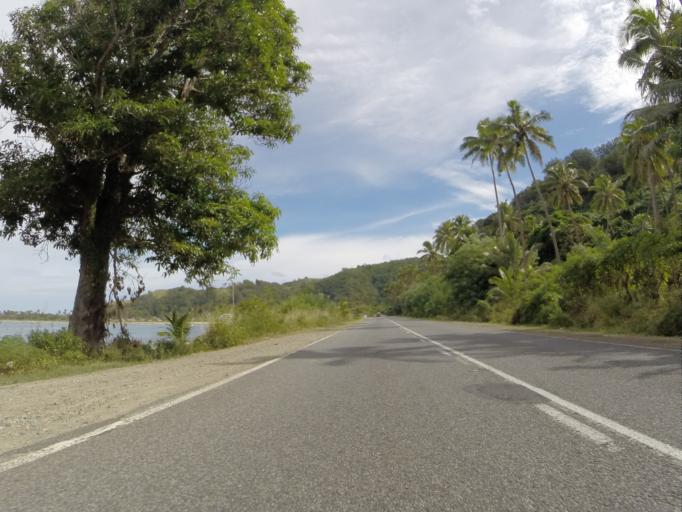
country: FJ
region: Western
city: Nadi
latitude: -18.1825
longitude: 177.6091
